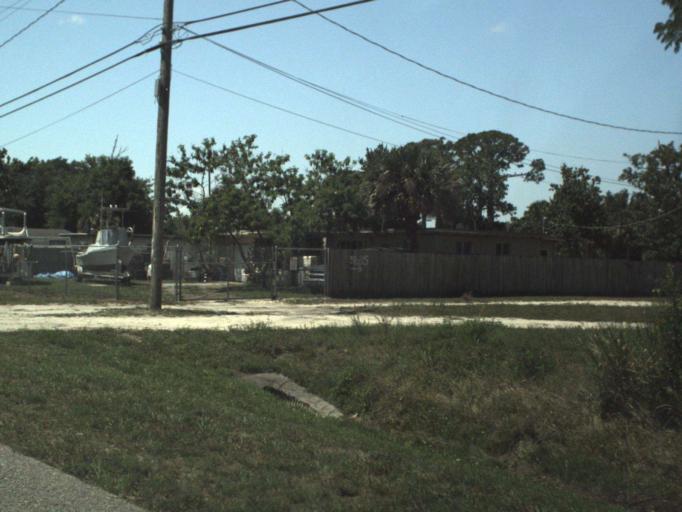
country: US
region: Florida
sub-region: Brevard County
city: Sharpes
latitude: 28.4587
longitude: -80.7096
